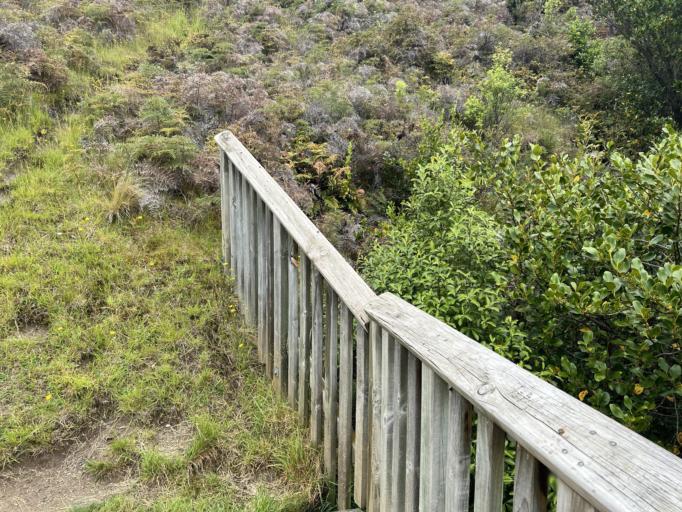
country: NZ
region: Otago
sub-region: Queenstown-Lakes District
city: Wanaka
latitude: -44.6466
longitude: 168.9650
